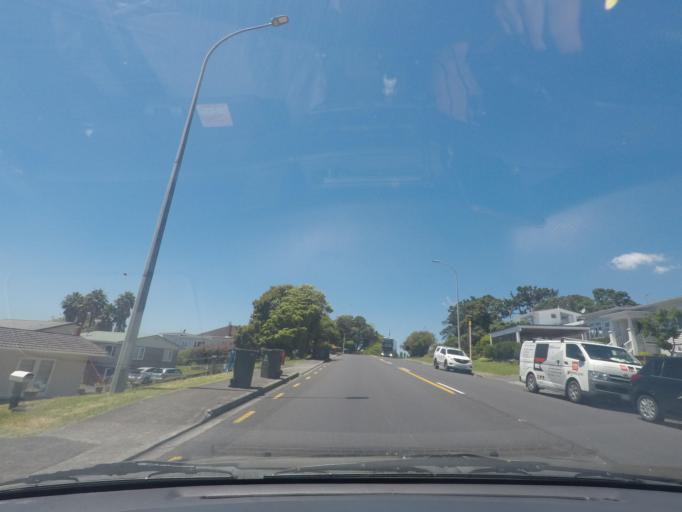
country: NZ
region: Auckland
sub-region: Auckland
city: Auckland
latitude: -36.9303
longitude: 174.7391
